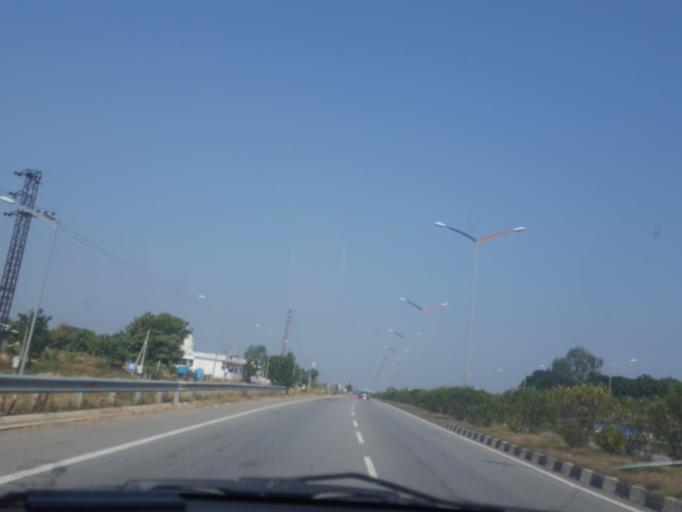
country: IN
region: Telangana
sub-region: Nizamabad District
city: Nizamabad
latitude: 18.5780
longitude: 78.2288
